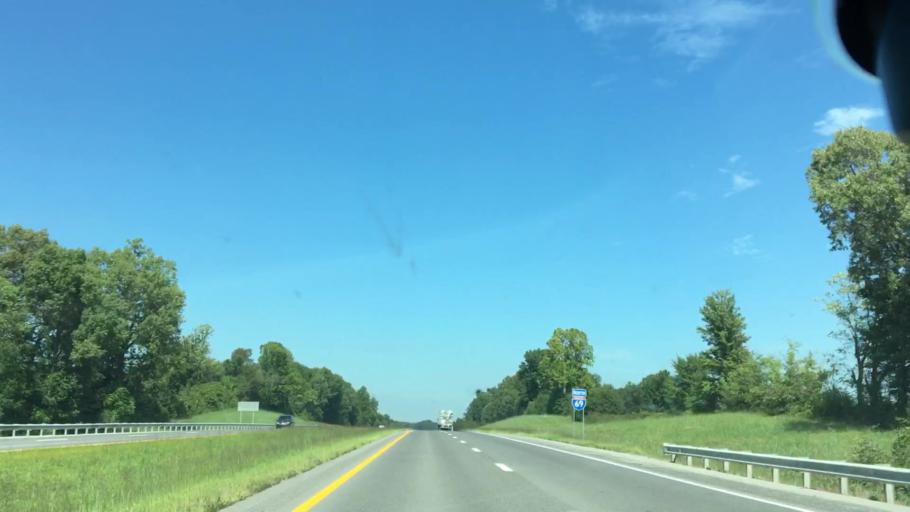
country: US
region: Kentucky
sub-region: Webster County
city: Sebree
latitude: 37.4959
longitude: -87.4752
